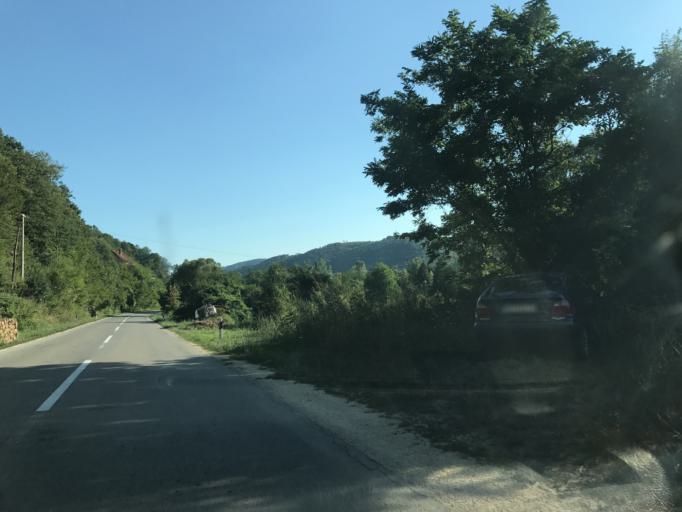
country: RO
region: Mehedinti
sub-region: Comuna Svinita
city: Svinita
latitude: 44.4200
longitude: 22.1760
